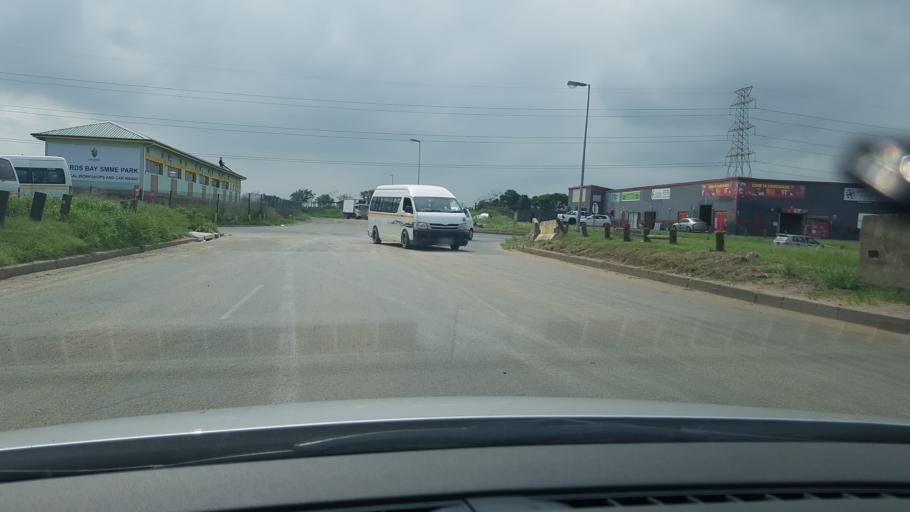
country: ZA
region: KwaZulu-Natal
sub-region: uThungulu District Municipality
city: Richards Bay
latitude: -28.7485
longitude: 32.0474
